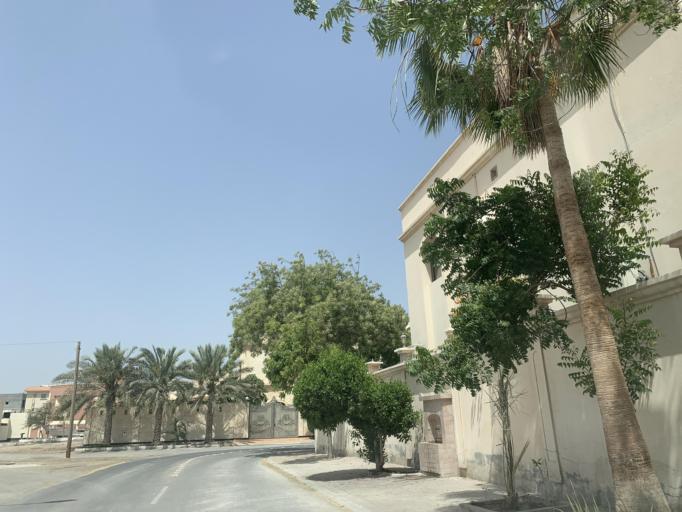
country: BH
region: Northern
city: Sitrah
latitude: 26.1557
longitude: 50.5869
